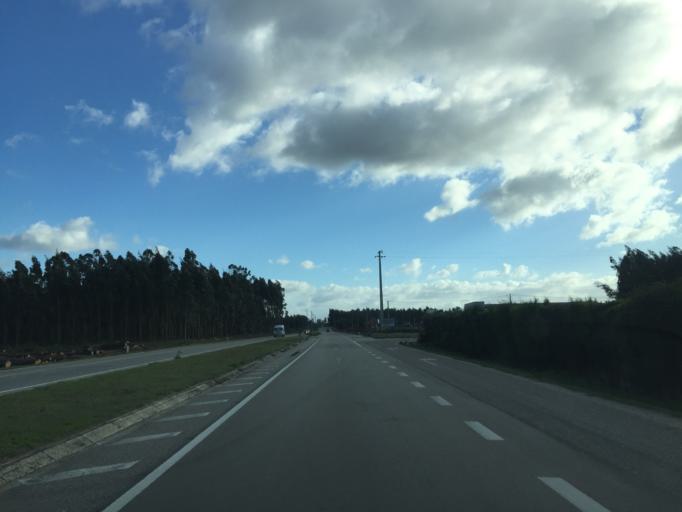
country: PT
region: Leiria
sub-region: Pombal
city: Lourical
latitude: 40.0103
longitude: -8.8070
